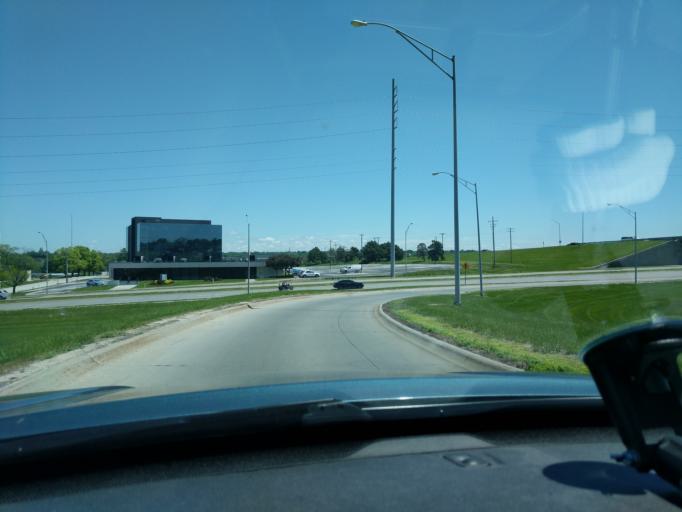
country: US
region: Nebraska
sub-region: Douglas County
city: Ralston
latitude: 41.2357
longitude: -96.0251
